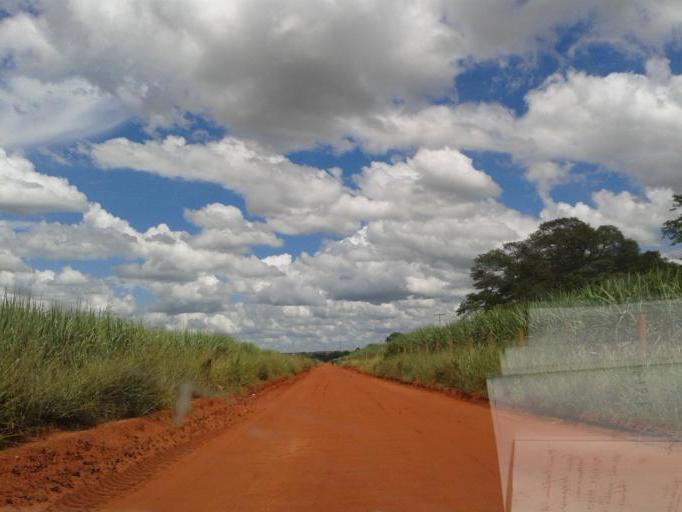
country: BR
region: Minas Gerais
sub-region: Santa Vitoria
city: Santa Vitoria
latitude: -18.8358
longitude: -50.0871
